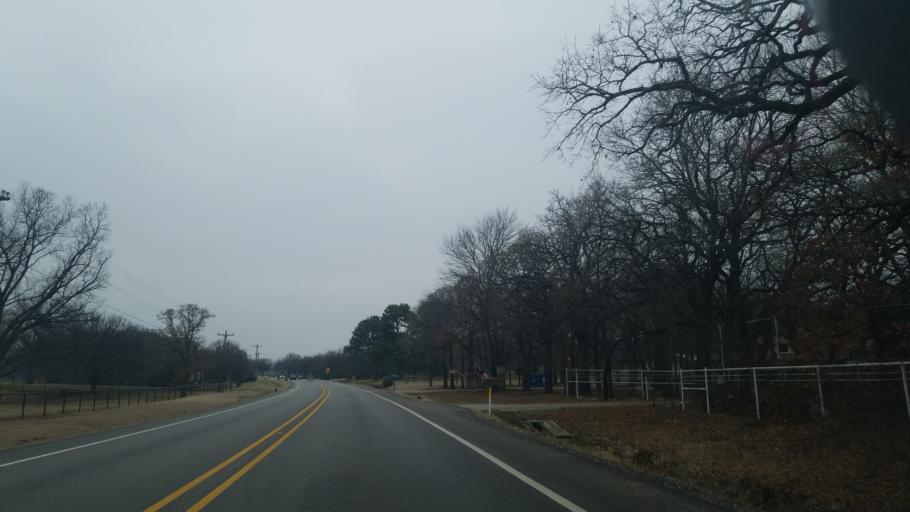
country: US
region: Texas
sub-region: Denton County
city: Argyle
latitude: 33.1419
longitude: -97.1485
